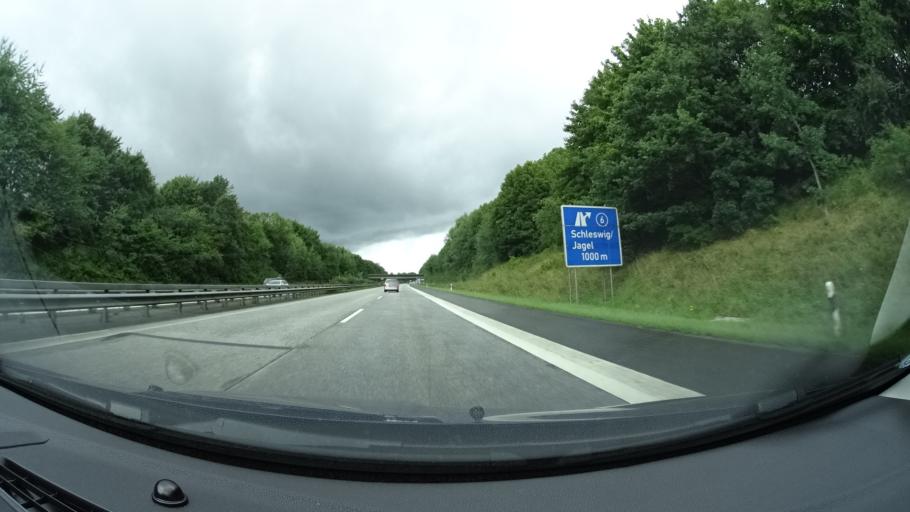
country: DE
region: Schleswig-Holstein
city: Selk
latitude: 54.4725
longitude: 9.5523
